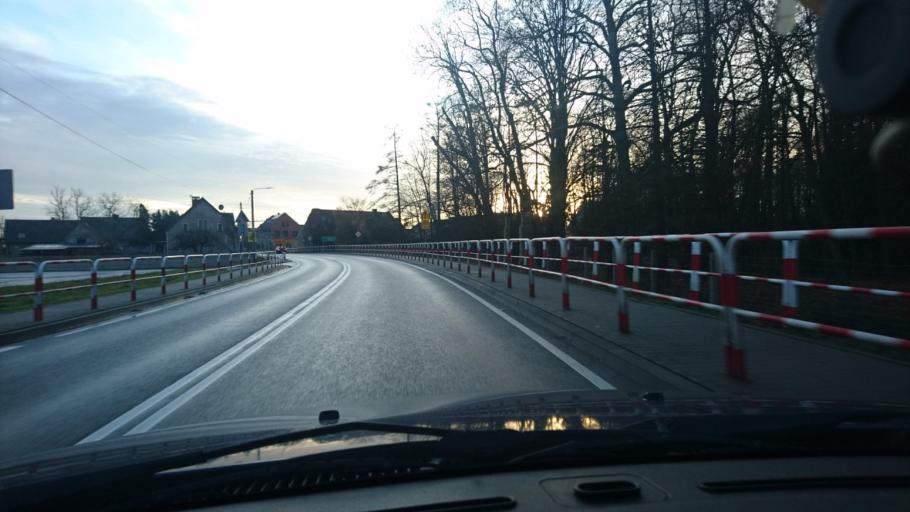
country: PL
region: Greater Poland Voivodeship
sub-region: Powiat kepinski
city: Opatow
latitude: 51.1807
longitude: 18.1439
